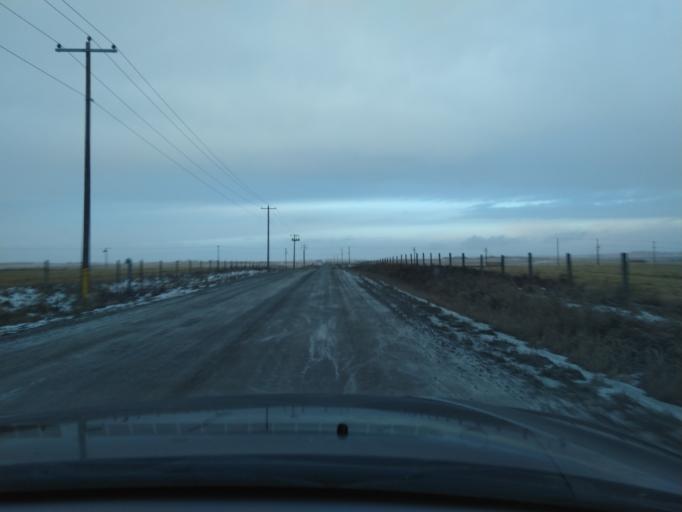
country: CA
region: Alberta
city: Airdrie
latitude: 51.1811
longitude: -114.0248
